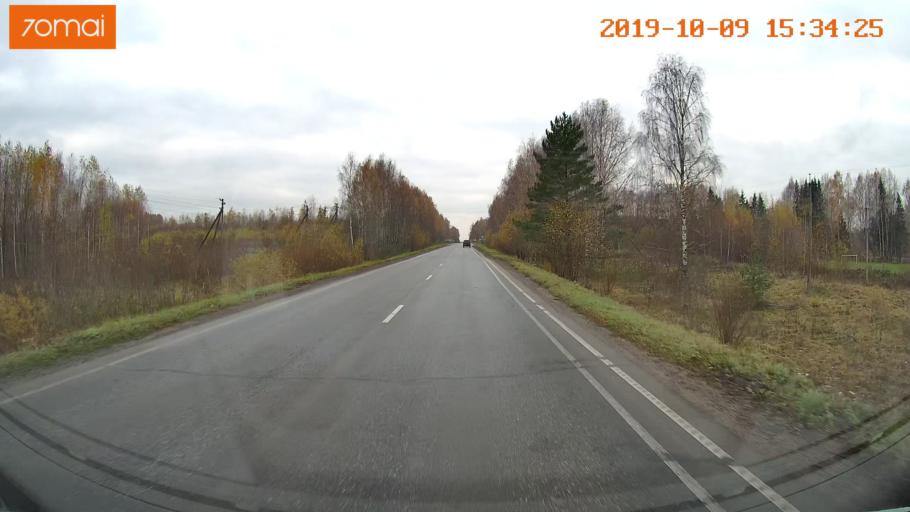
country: RU
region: Kostroma
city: Oktyabr'skiy
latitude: 57.9409
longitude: 41.2450
